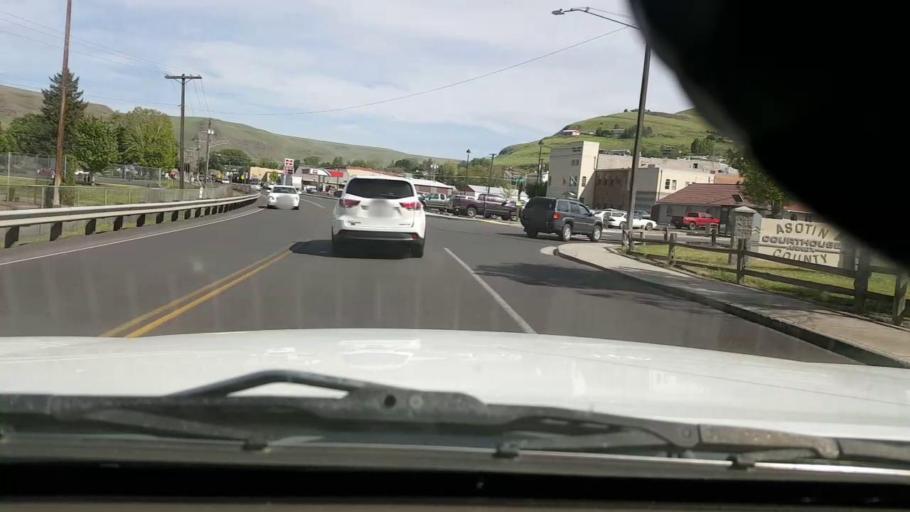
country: US
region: Washington
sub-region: Asotin County
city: Asotin
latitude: 46.3413
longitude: -117.0550
